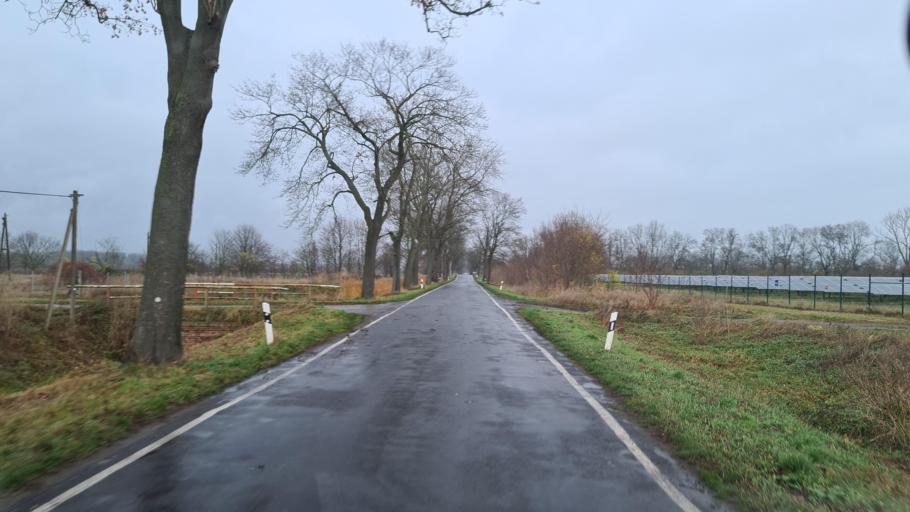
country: DE
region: Brandenburg
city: Nauen
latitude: 52.6560
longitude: 12.8047
